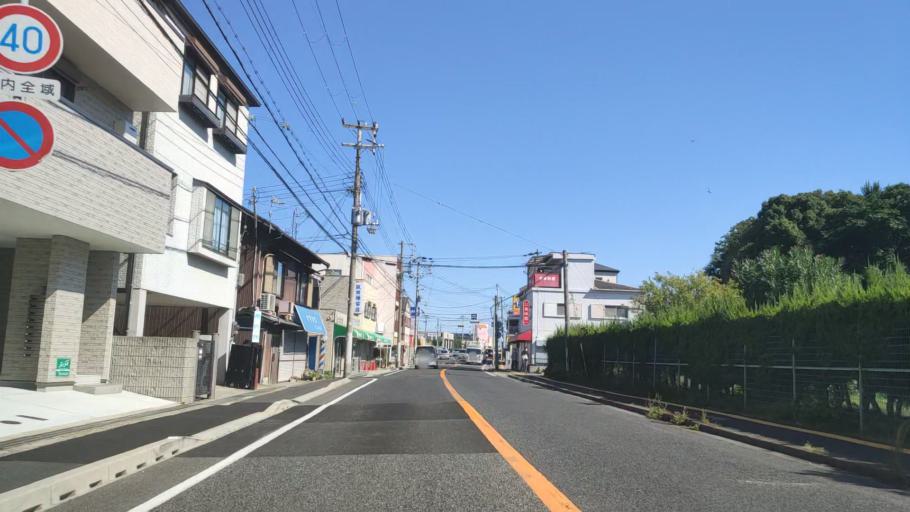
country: JP
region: Hyogo
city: Akashi
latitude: 34.6544
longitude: 134.9886
